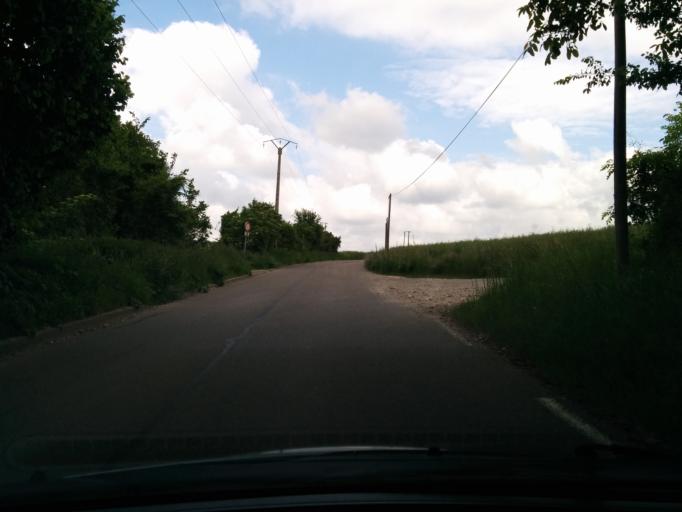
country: FR
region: Ile-de-France
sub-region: Departement des Yvelines
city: Oinville-sur-Montcient
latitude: 49.0256
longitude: 1.8141
